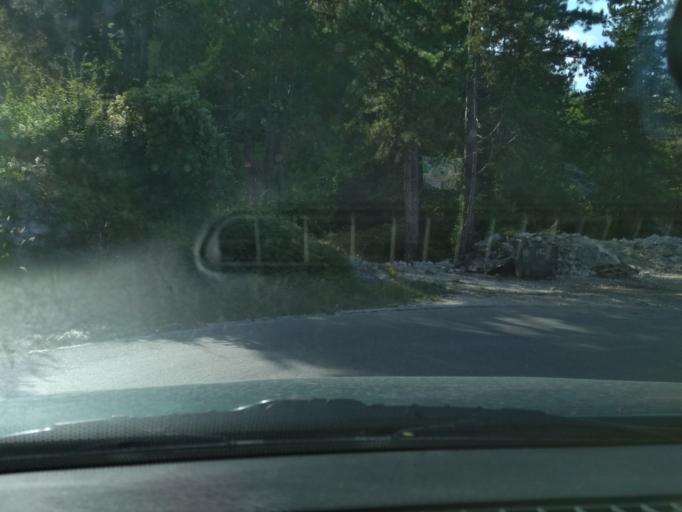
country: ME
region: Cetinje
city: Cetinje
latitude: 42.3897
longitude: 18.9017
